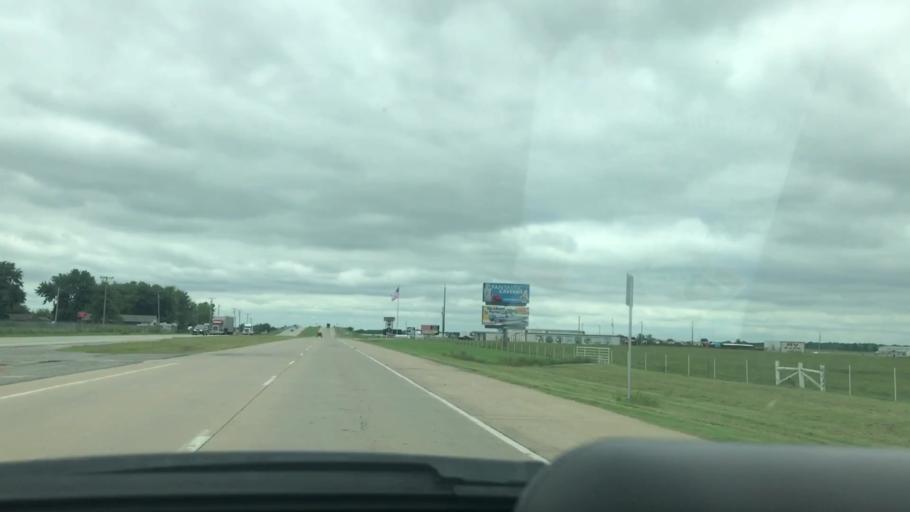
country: US
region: Oklahoma
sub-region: Craig County
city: Vinita
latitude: 36.5502
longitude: -95.2201
